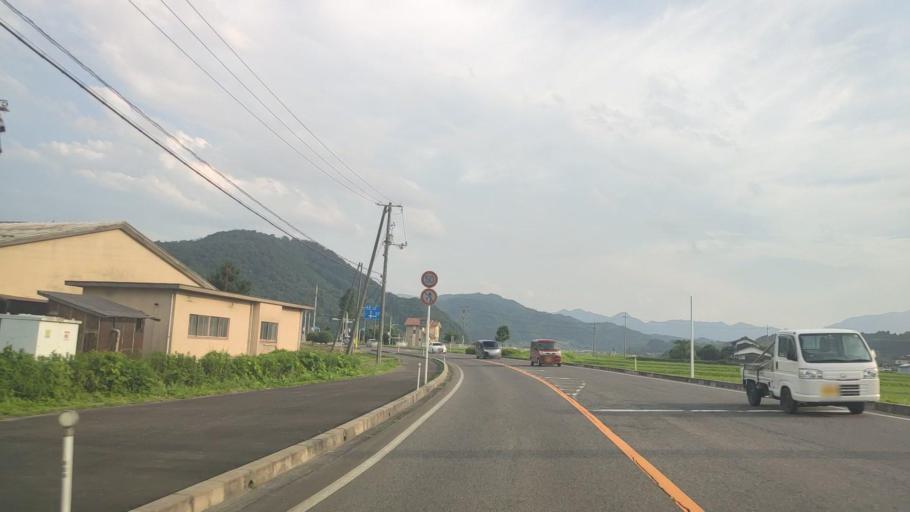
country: JP
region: Tottori
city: Kurayoshi
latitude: 35.3916
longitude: 133.7795
